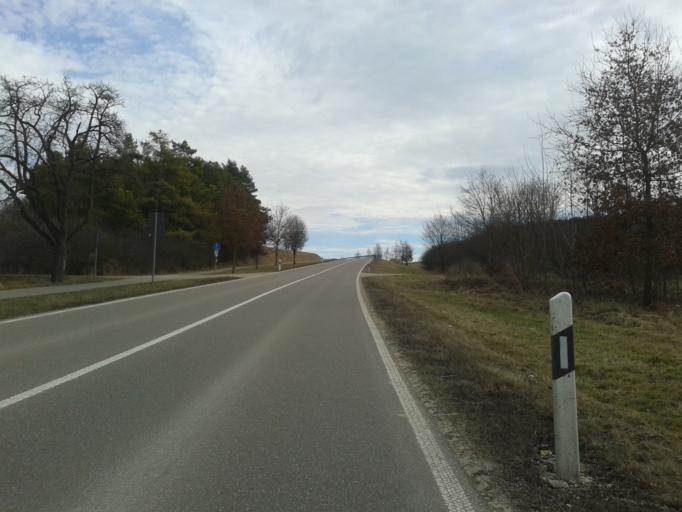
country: DE
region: Baden-Wuerttemberg
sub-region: Tuebingen Region
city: Allmendingen
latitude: 48.3232
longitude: 9.7465
